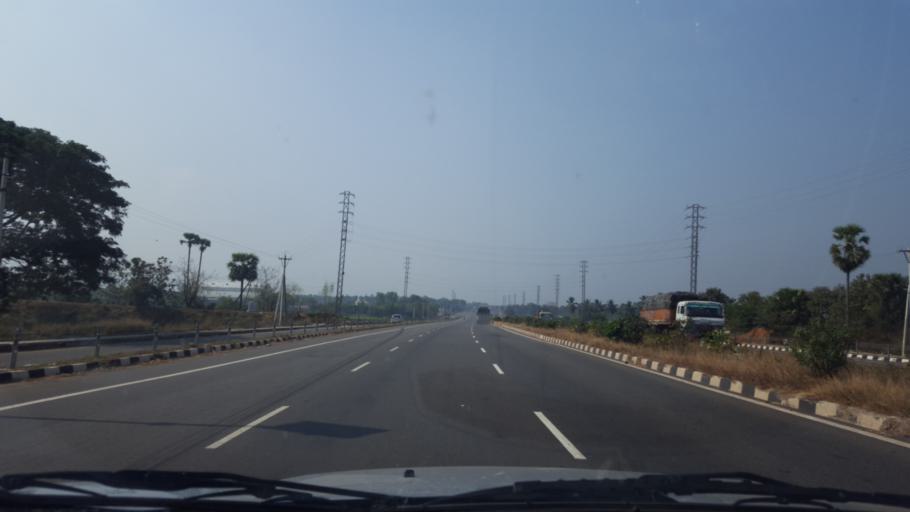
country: IN
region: Andhra Pradesh
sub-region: Vishakhapatnam
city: Bhimunipatnam
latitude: 18.0044
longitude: 83.4791
